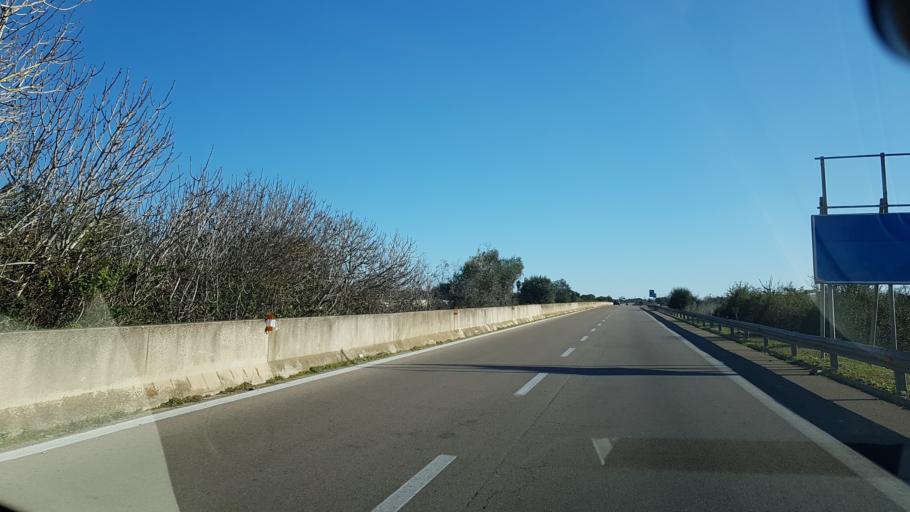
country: IT
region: Apulia
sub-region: Provincia di Lecce
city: Taviano
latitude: 40.0089
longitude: 18.0544
